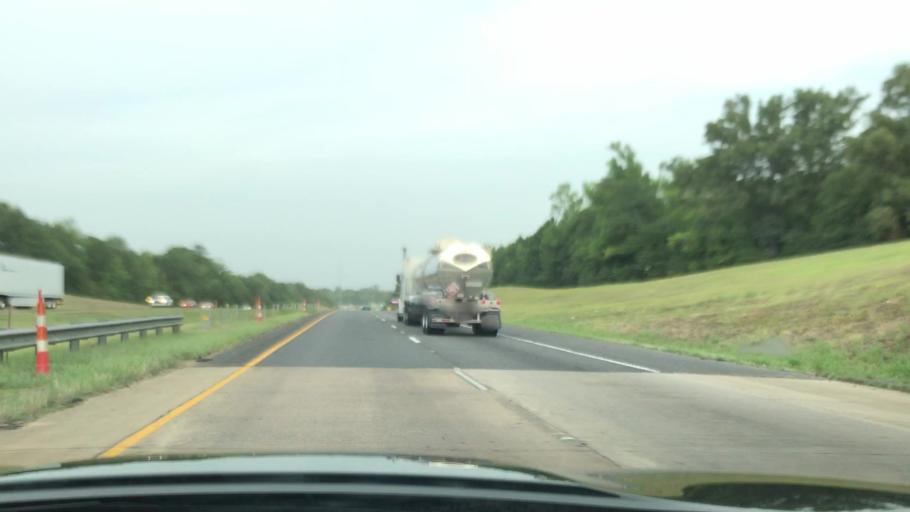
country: US
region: Louisiana
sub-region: Caddo Parish
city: Greenwood
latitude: 32.4519
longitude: -94.0115
